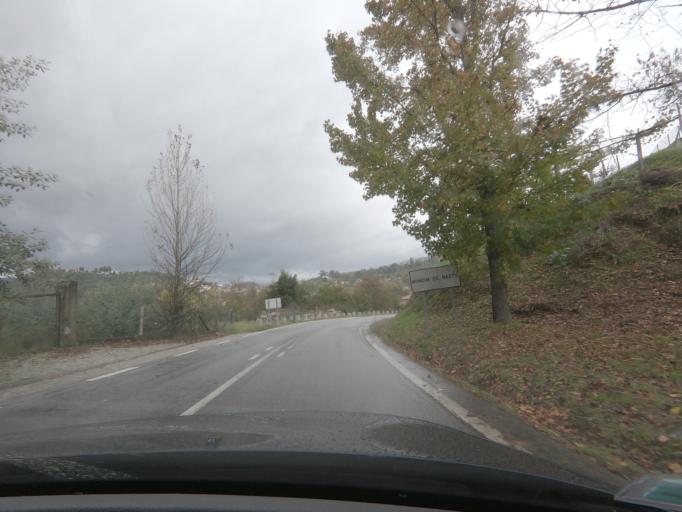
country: PT
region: Vila Real
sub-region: Mondim de Basto
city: Mondim de Basto
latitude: 41.3991
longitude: -7.9605
